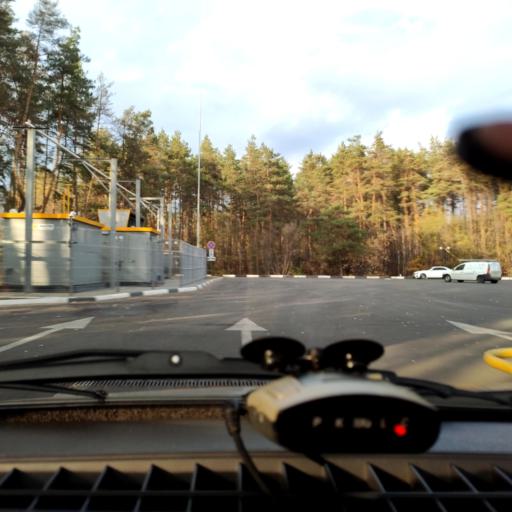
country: RU
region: Voronezj
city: Podgornoye
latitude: 51.7330
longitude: 39.1809
